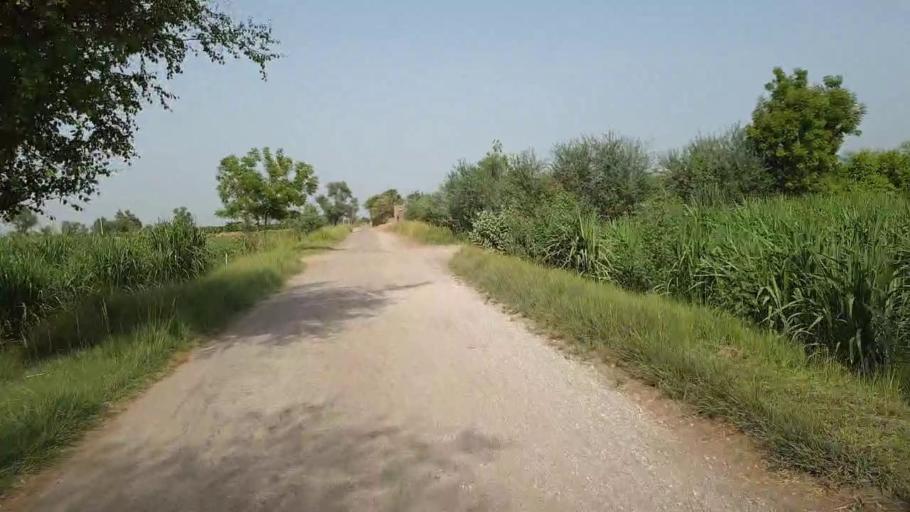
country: PK
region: Sindh
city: Daur
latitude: 26.3227
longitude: 68.1592
